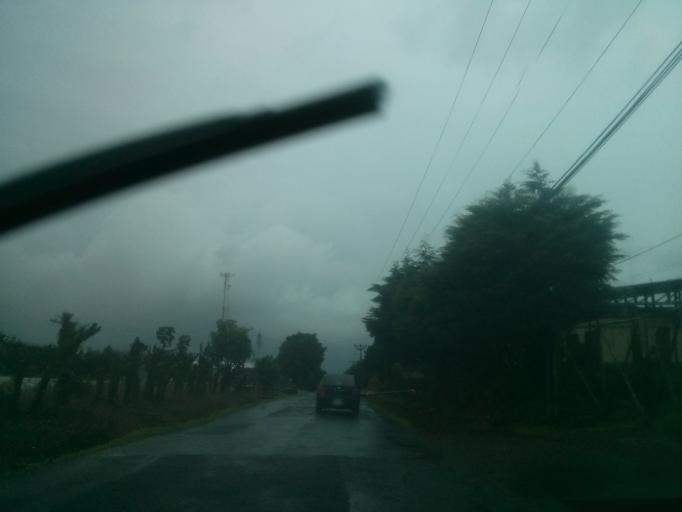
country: CR
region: Alajuela
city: Sabanilla
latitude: 10.1553
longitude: -84.1946
